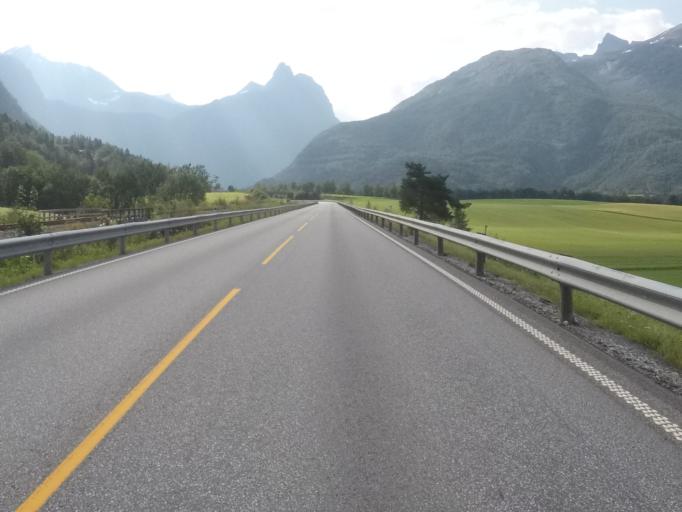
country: NO
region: More og Romsdal
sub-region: Rauma
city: Andalsnes
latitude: 62.5434
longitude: 7.7193
